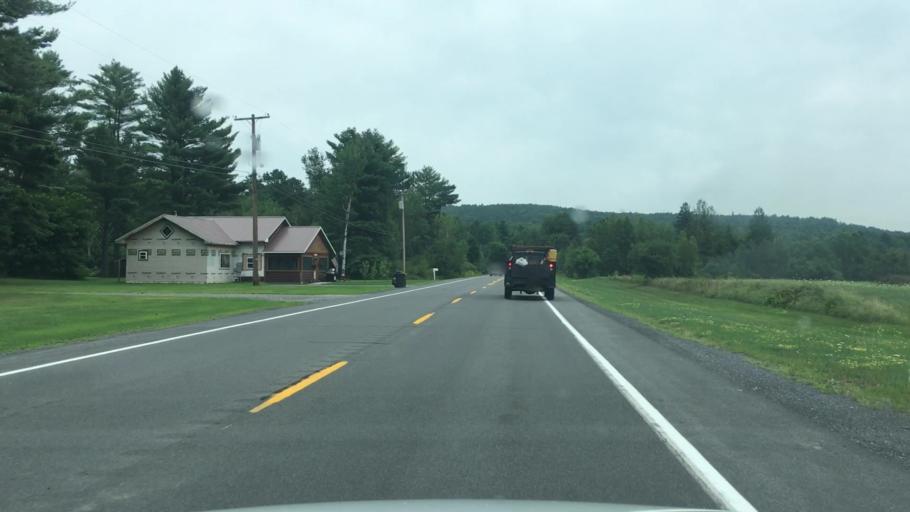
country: US
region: New York
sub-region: Essex County
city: Keeseville
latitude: 44.4618
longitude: -73.6014
